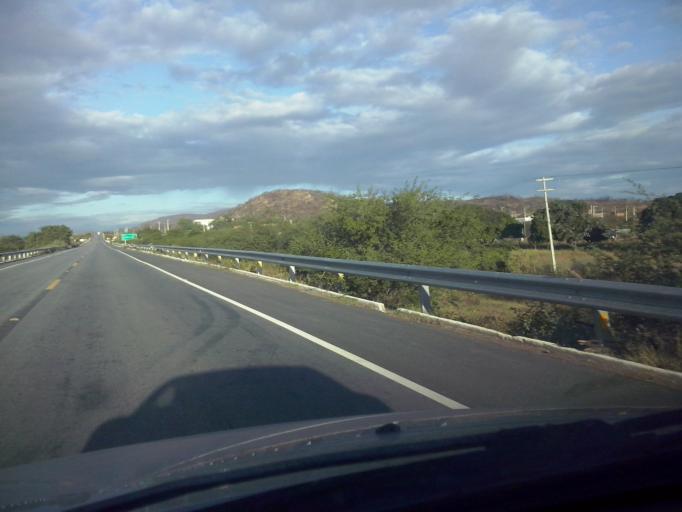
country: BR
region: Paraiba
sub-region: Patos
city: Patos
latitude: -6.9062
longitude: -37.5125
